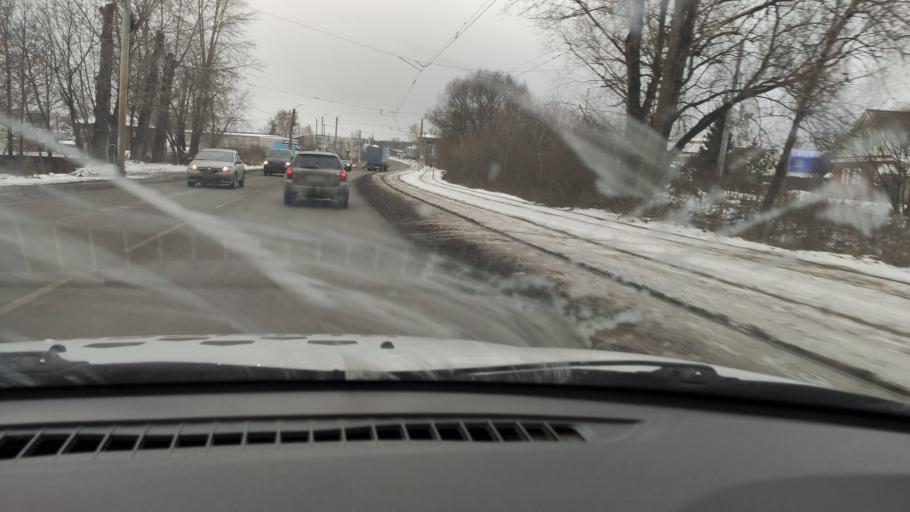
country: RU
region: Perm
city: Kondratovo
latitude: 57.9563
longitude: 56.1332
